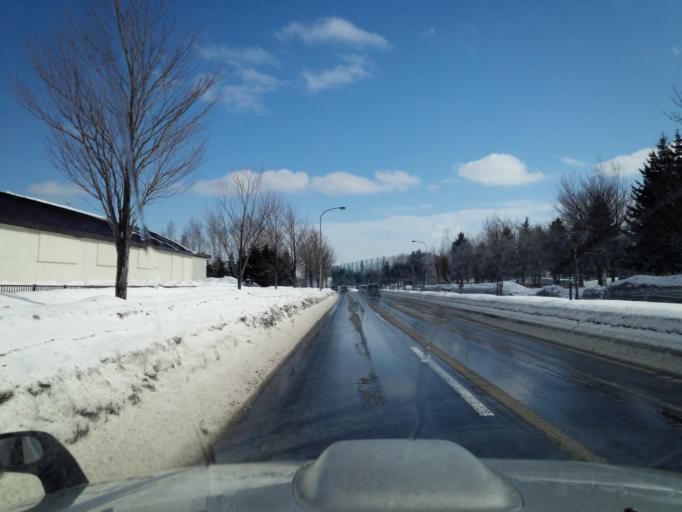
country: JP
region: Hokkaido
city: Kitahiroshima
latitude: 42.9924
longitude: 141.4545
